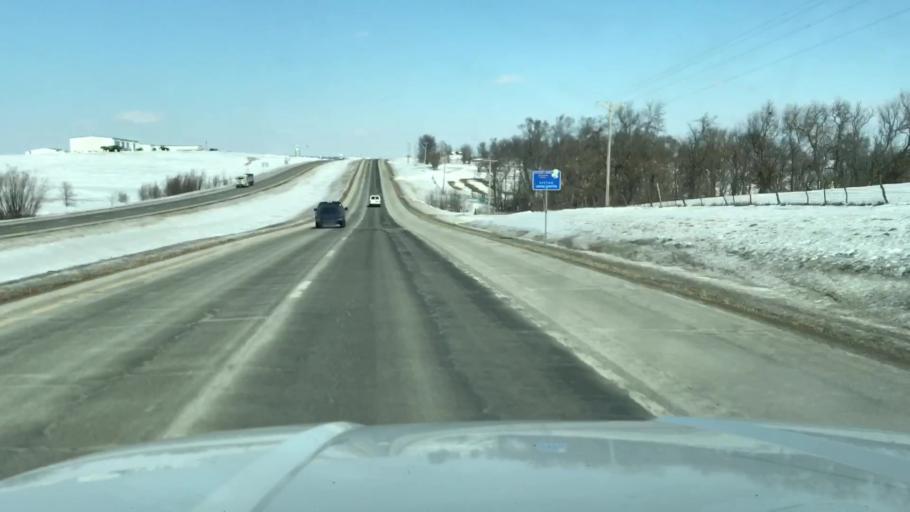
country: US
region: Missouri
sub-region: Nodaway County
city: Maryville
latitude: 40.2940
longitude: -94.8750
